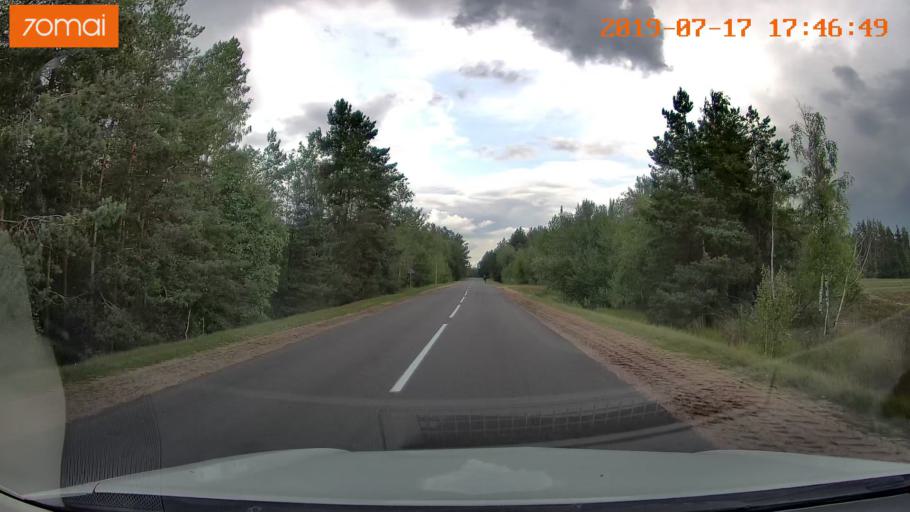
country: BY
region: Mogilev
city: Hlusha
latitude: 53.1025
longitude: 28.8343
